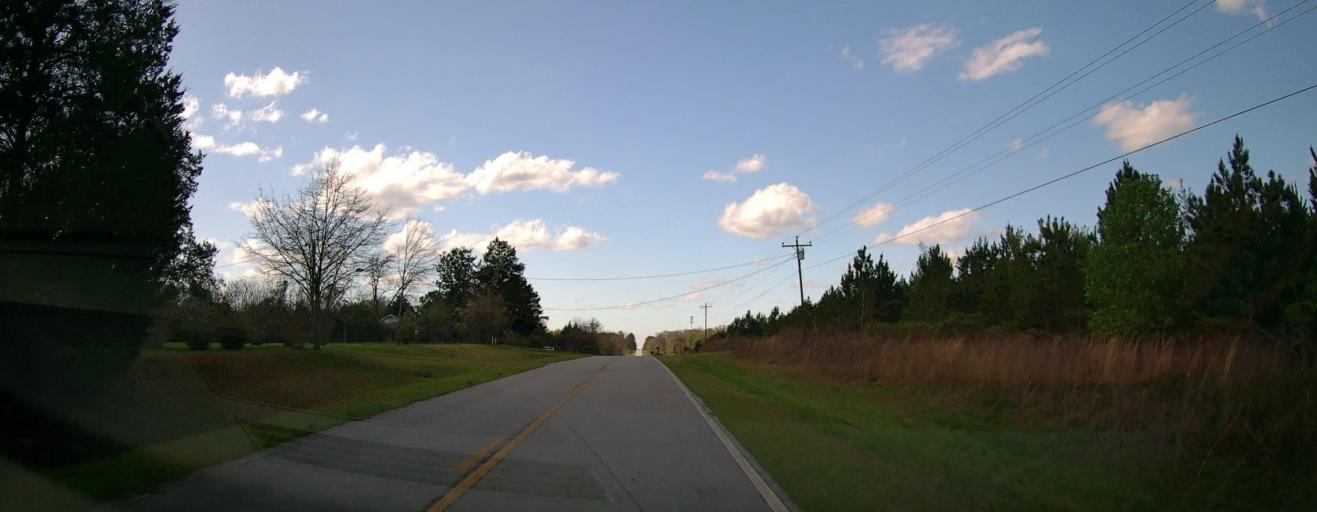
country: US
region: Georgia
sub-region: Wilkinson County
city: Gordon
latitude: 32.8302
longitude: -83.4282
